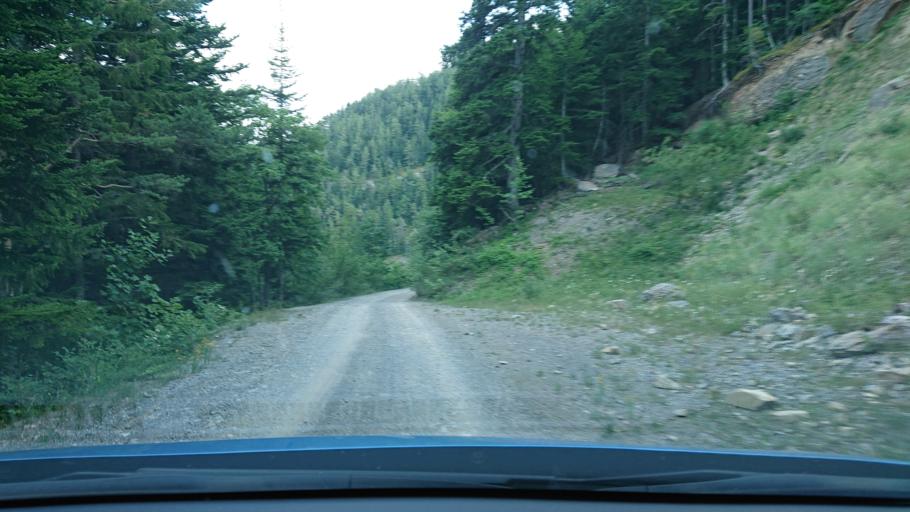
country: FR
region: Rhone-Alpes
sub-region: Departement de l'Isere
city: Mens
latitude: 44.7949
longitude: 5.8909
